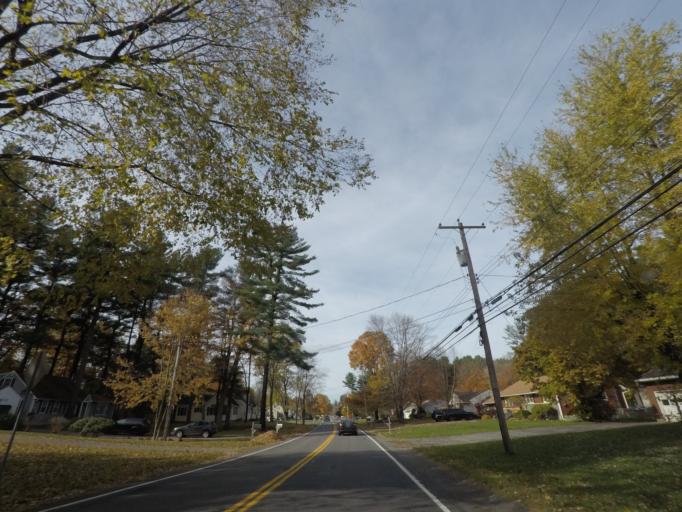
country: US
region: New York
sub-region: Schenectady County
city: Rotterdam
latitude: 42.7503
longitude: -73.9361
